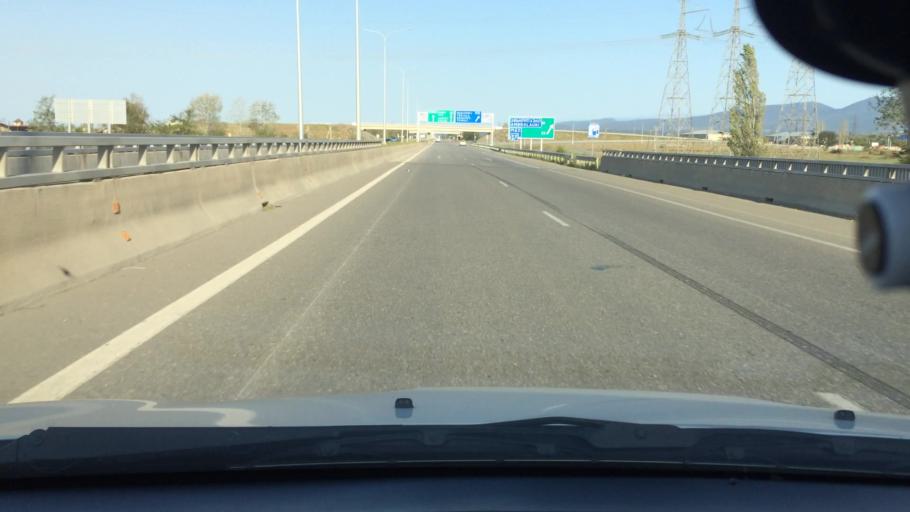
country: GE
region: Imereti
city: Zestap'oni
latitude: 42.1564
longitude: 42.9541
